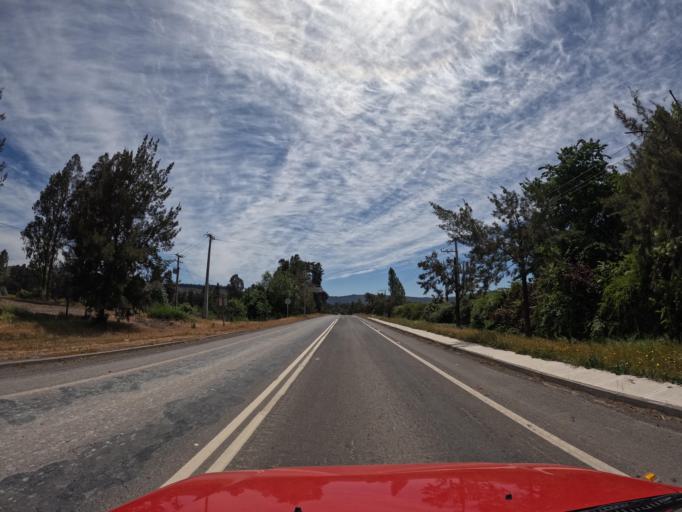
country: CL
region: Maule
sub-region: Provincia de Talca
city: Talca
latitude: -35.2968
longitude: -71.5275
